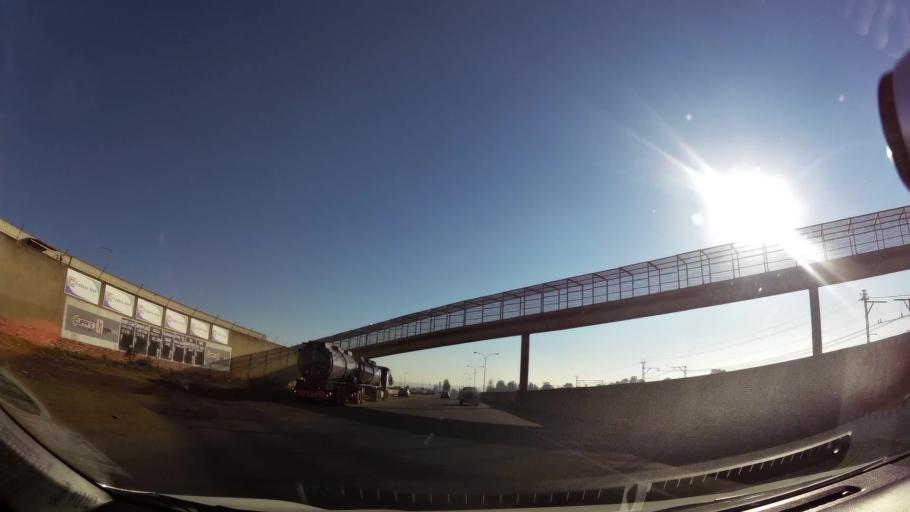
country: ZA
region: Gauteng
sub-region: Ekurhuleni Metropolitan Municipality
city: Germiston
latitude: -26.3246
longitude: 28.1388
